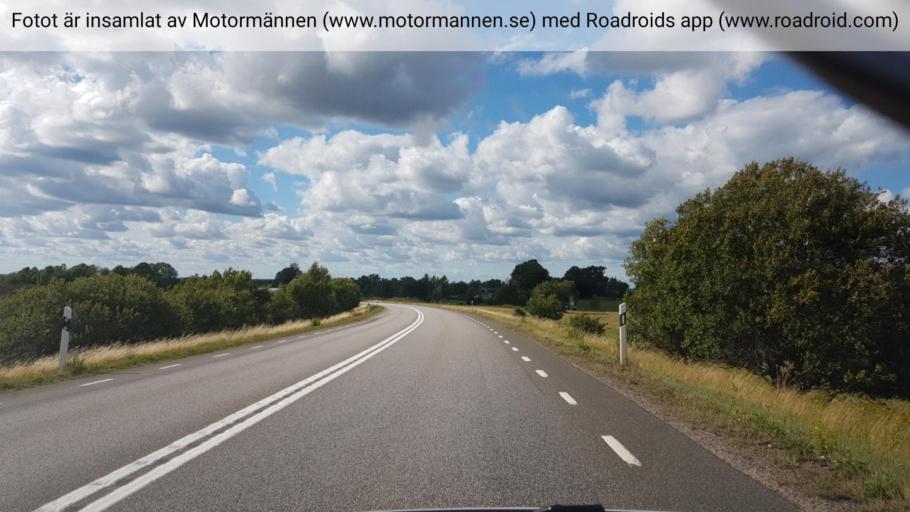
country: SE
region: Vaestra Goetaland
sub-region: Falkopings Kommun
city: Falkoeping
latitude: 58.2387
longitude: 13.5442
